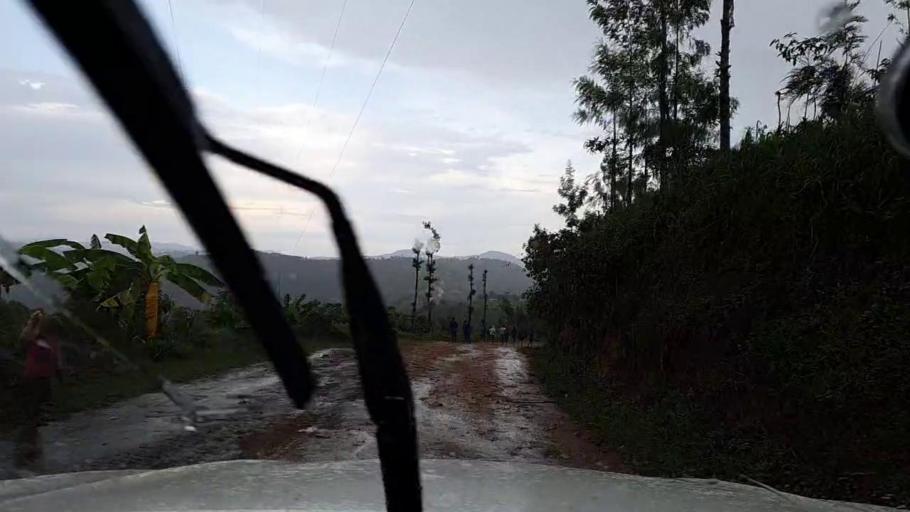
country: BI
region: Kayanza
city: Kayanza
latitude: -2.7755
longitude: 29.5400
